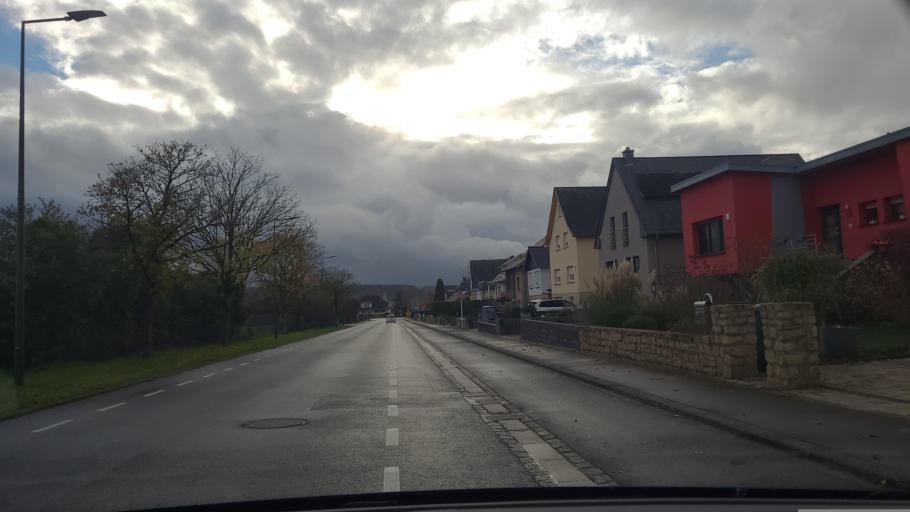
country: LU
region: Luxembourg
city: Hautcharage
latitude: 49.5738
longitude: 5.9032
